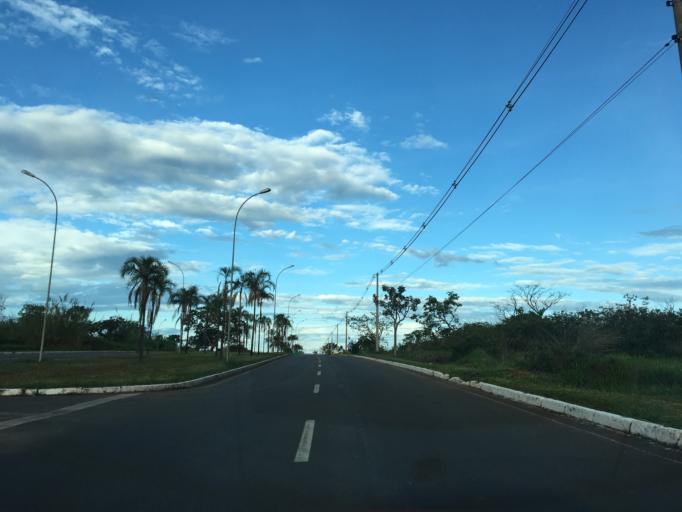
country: BR
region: Federal District
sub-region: Brasilia
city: Brasilia
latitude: -15.8102
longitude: -47.8430
